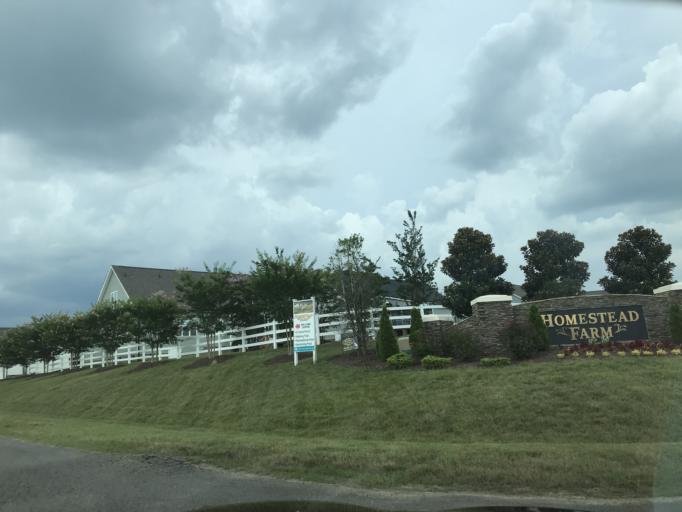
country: US
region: North Carolina
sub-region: Johnston County
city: Four Oaks
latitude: 35.5149
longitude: -78.5317
